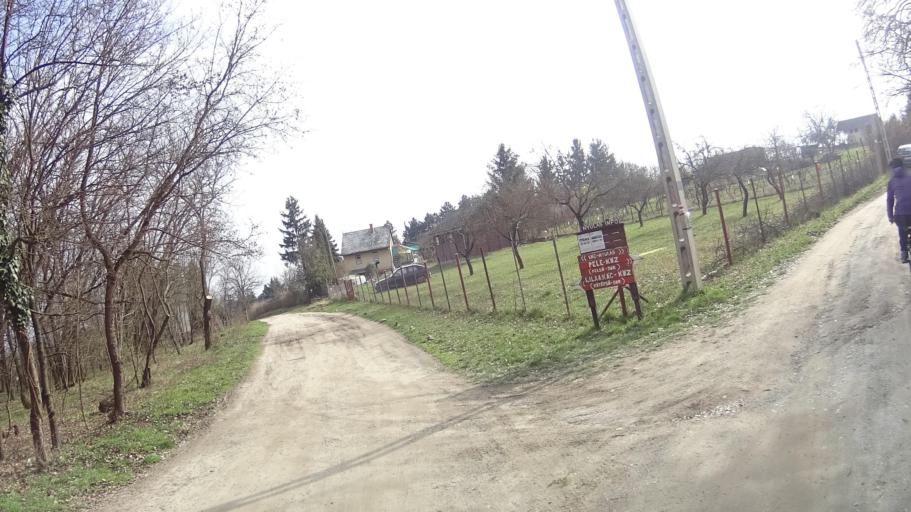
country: HU
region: Pest
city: Veroce
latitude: 47.8267
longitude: 19.0844
